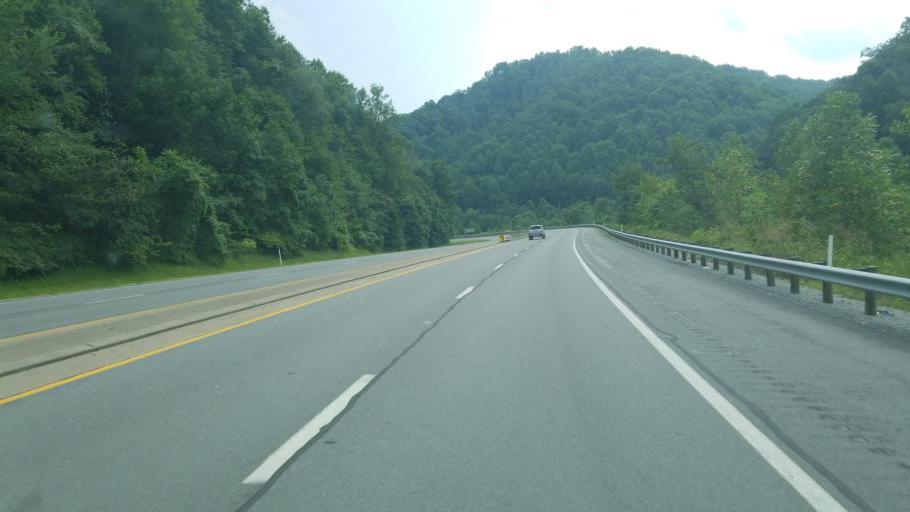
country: US
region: West Virginia
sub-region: Logan County
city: Mount Gay-Shamrock
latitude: 37.8152
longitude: -82.0647
